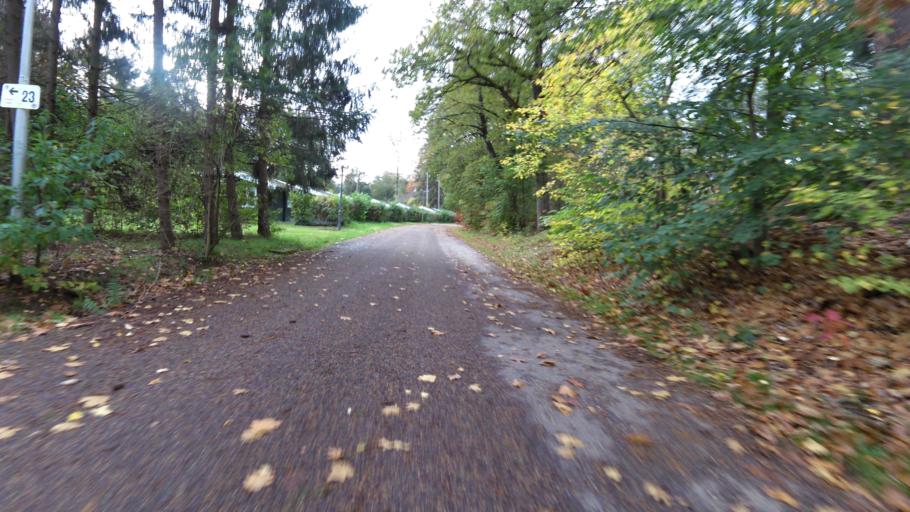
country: NL
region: Gelderland
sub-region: Gemeente Nunspeet
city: Nunspeet
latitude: 52.3298
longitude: 5.8215
